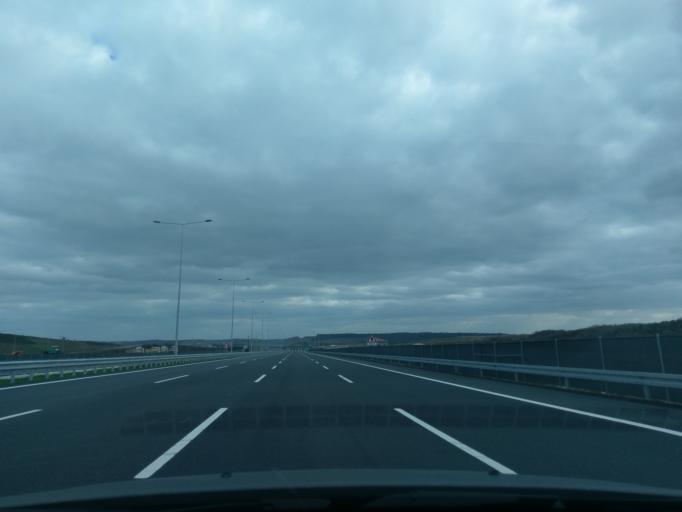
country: TR
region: Istanbul
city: Durusu
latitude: 41.2441
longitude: 28.7032
